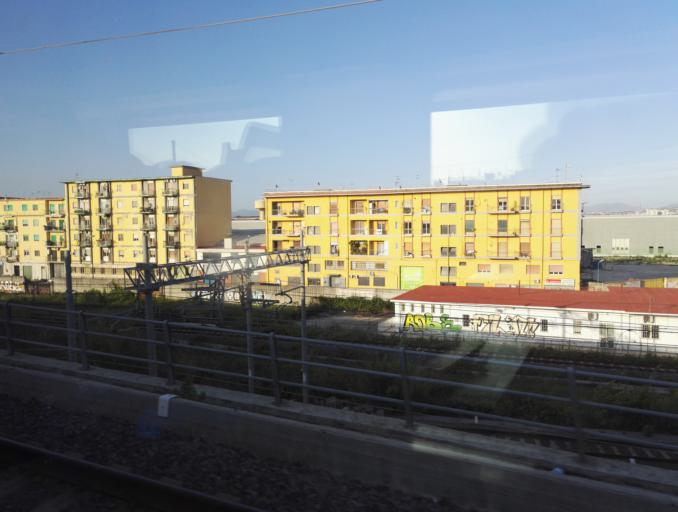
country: IT
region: Campania
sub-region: Provincia di Napoli
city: Arpino
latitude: 40.8601
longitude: 14.2970
